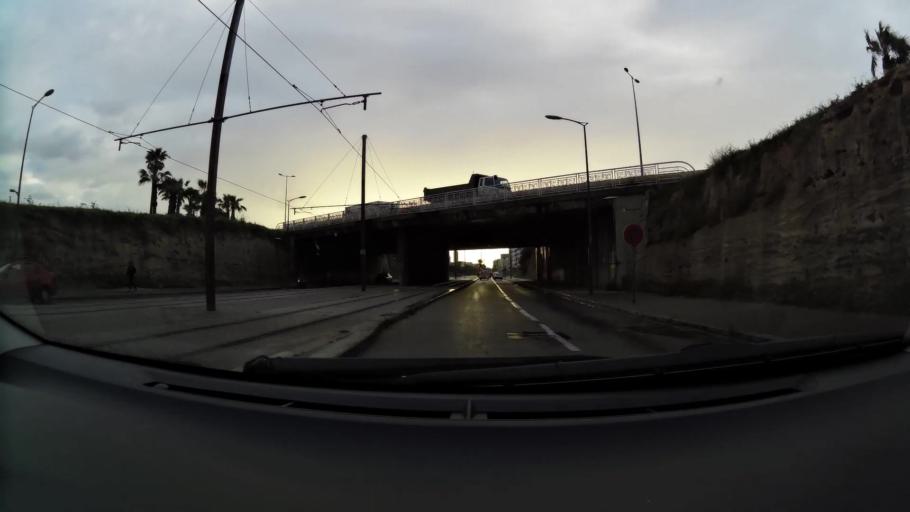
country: MA
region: Grand Casablanca
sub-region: Casablanca
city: Casablanca
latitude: 33.5785
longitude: -7.5552
